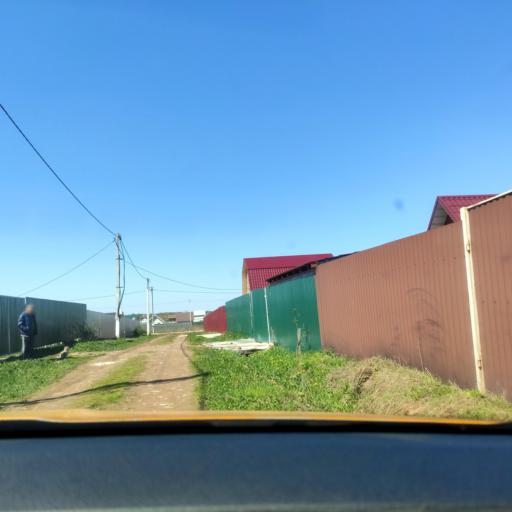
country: RU
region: Moskovskaya
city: Beloozerskiy
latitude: 55.3729
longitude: 38.4003
